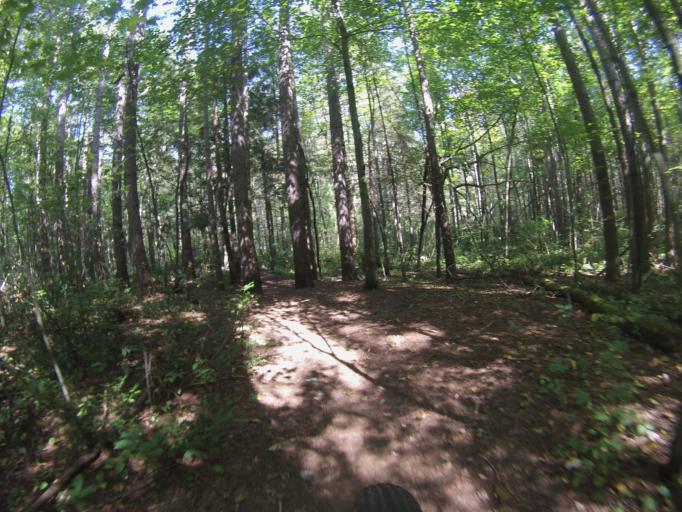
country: CA
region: Ontario
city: Ottawa
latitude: 45.3556
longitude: -75.6185
